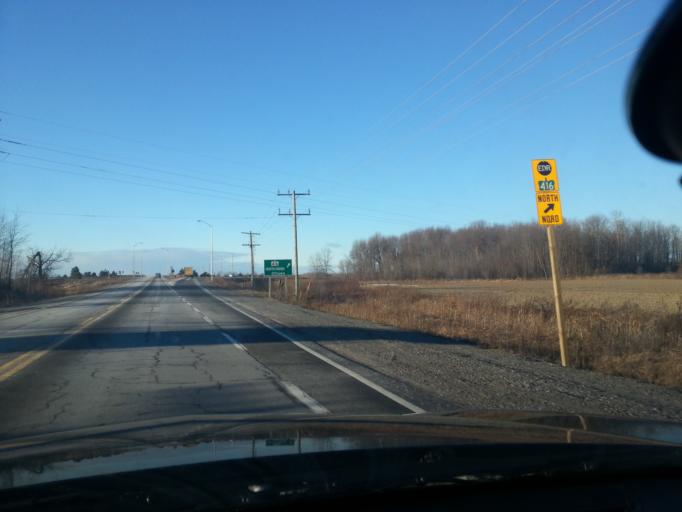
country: CA
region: Ontario
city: Bells Corners
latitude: 45.2118
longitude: -75.7319
